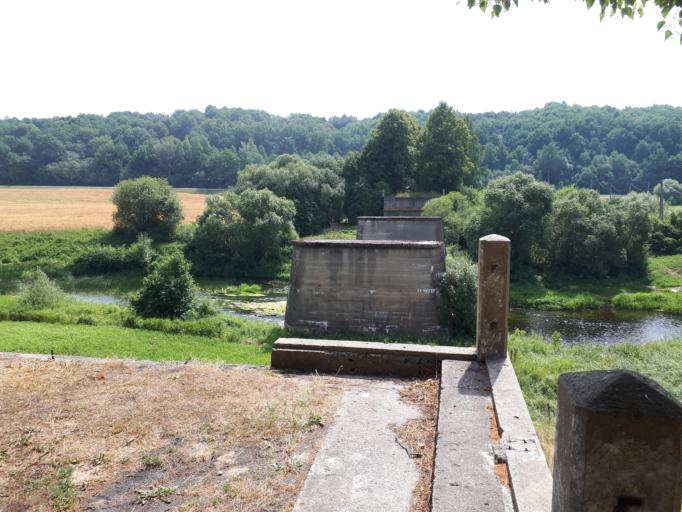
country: LT
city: Vilkija
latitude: 55.0811
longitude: 23.4275
